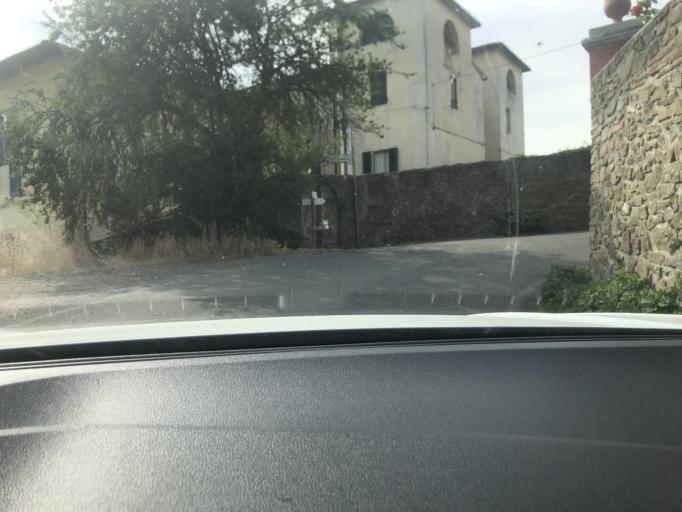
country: IT
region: Tuscany
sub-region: Provincia di Pistoia
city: Larciano
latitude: 43.8236
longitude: 10.9083
